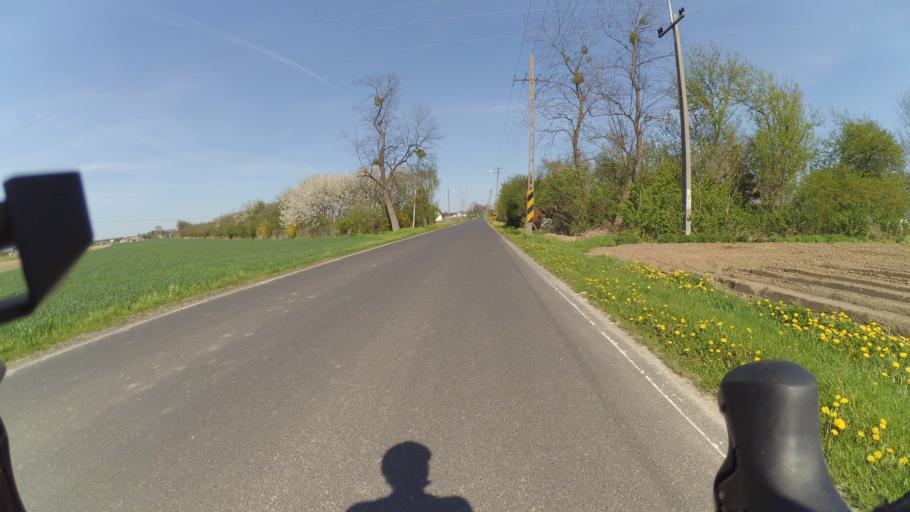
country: PL
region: Masovian Voivodeship
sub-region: Powiat warszawski zachodni
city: Leszno
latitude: 52.2483
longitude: 20.5562
